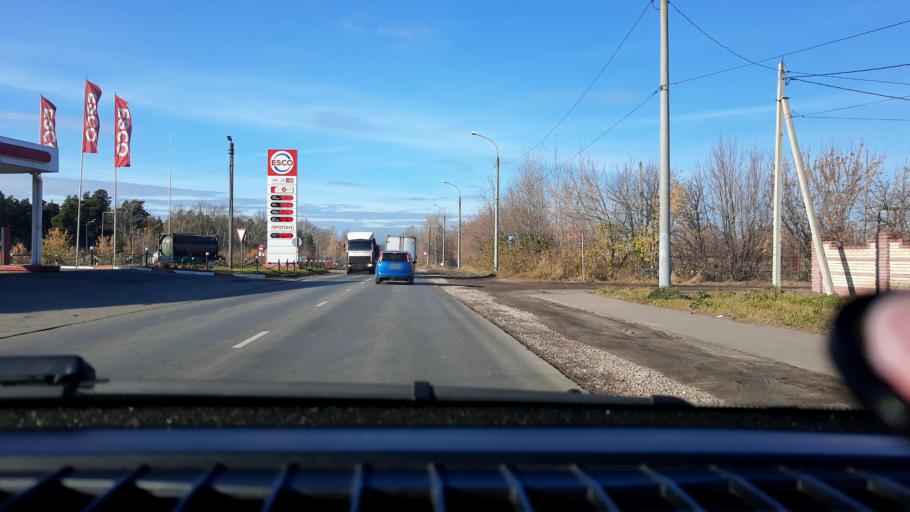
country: RU
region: Nizjnij Novgorod
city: Kstovo
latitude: 56.1655
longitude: 44.1859
